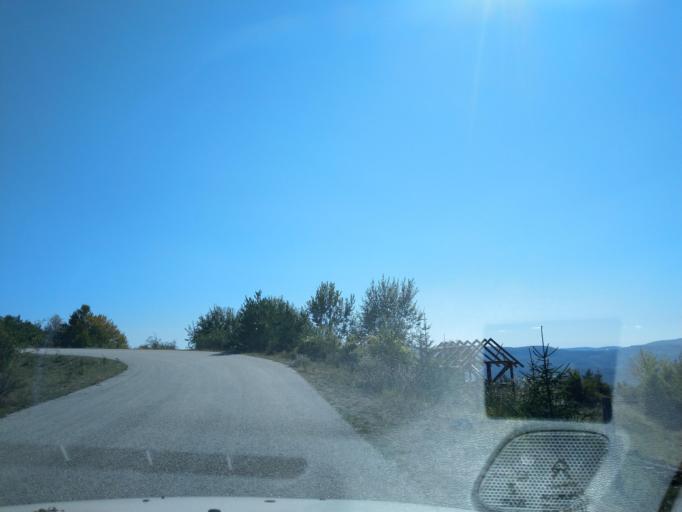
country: RS
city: Sokolovica
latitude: 43.2508
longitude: 20.3099
